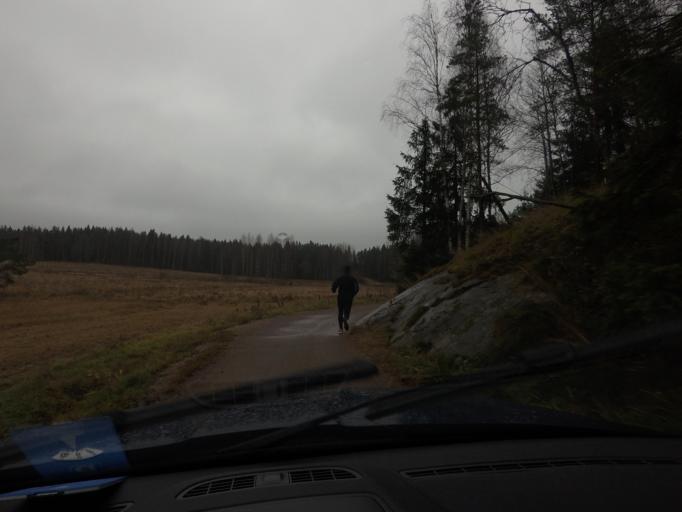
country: FI
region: Uusimaa
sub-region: Helsinki
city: Espoo
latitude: 60.1880
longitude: 24.6831
